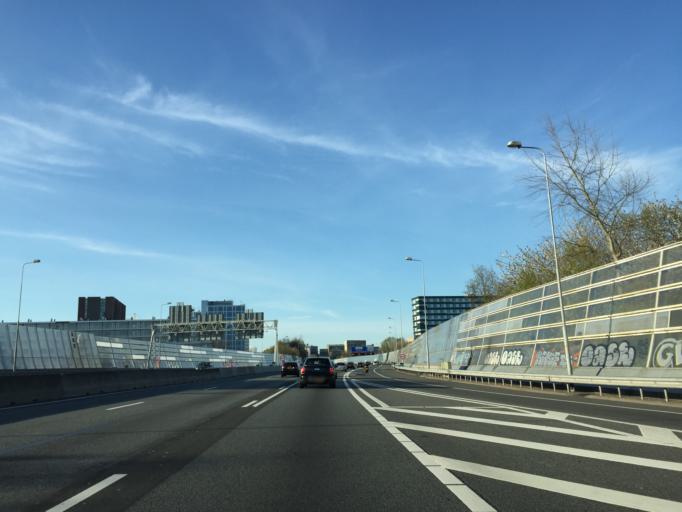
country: NL
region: North Holland
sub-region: Gemeente Amstelveen
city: Amstelveen
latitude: 52.3478
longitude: 4.8413
